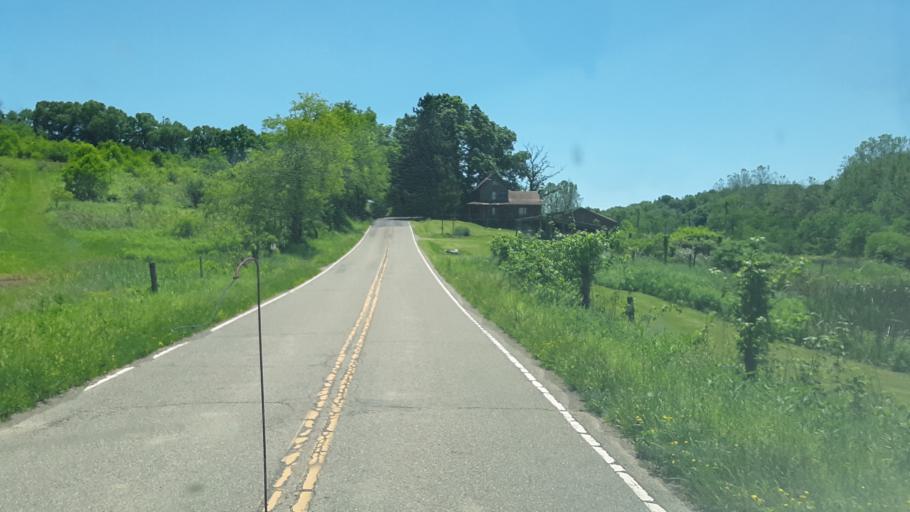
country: US
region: Ohio
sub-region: Coshocton County
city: Coshocton
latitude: 40.2777
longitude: -81.9842
